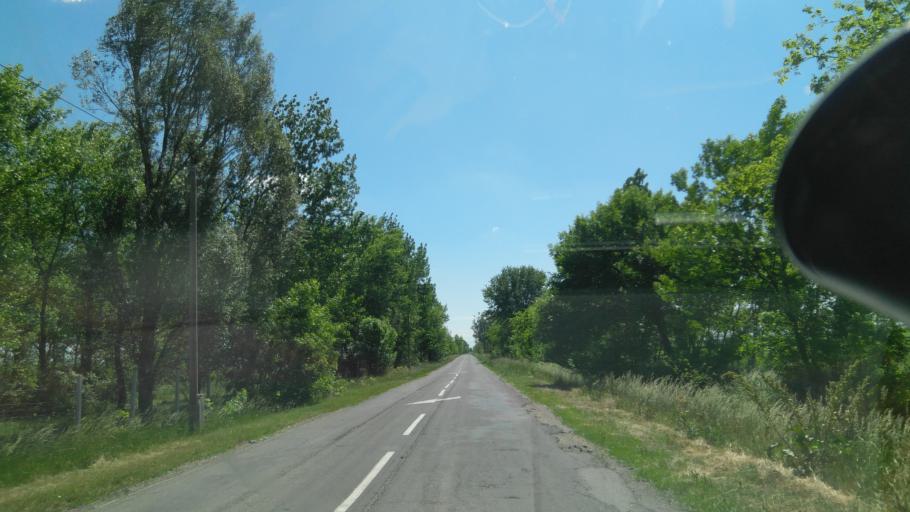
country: HU
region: Bekes
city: Kunagota
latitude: 46.4145
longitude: 21.0438
